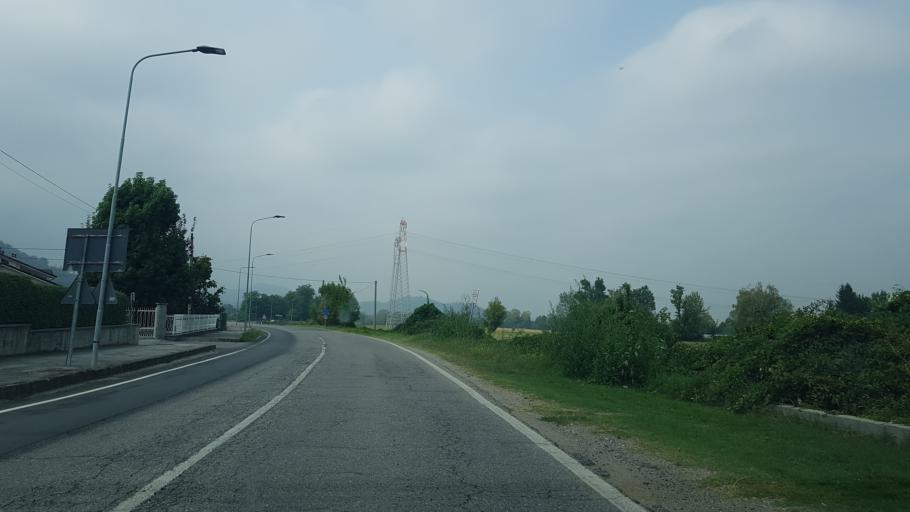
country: IT
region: Piedmont
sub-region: Provincia di Cuneo
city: Chiusa di Pesio
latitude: 44.3299
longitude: 7.6670
